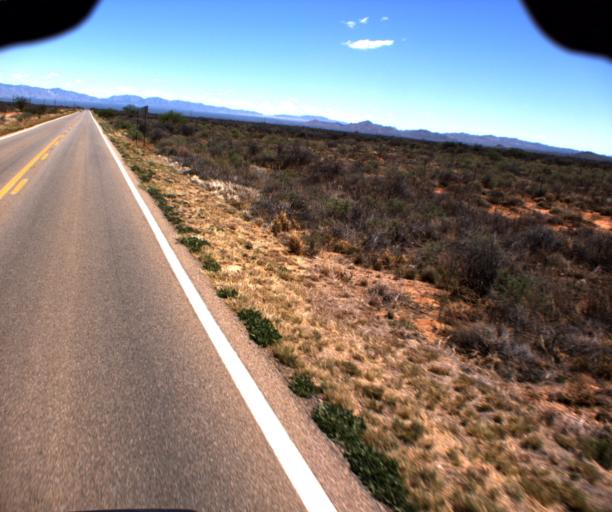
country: US
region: Arizona
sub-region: Cochise County
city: Huachuca City
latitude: 31.6974
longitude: -110.3037
